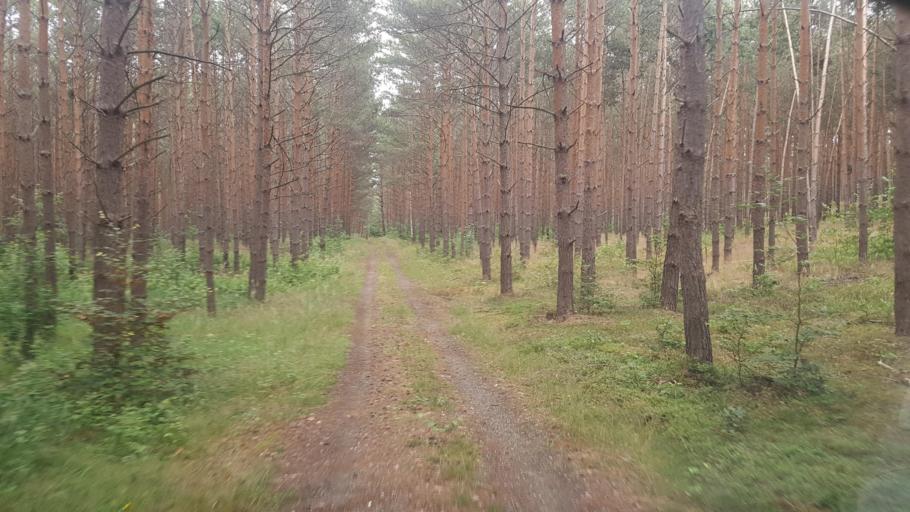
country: DE
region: Brandenburg
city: Crinitz
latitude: 51.7436
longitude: 13.7854
